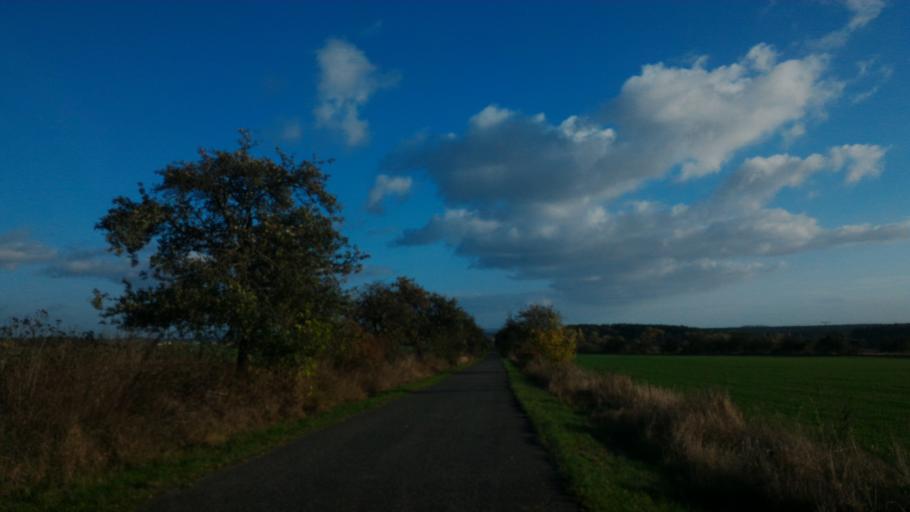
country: CZ
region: Central Bohemia
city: Bela pod Bezdezem
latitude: 50.5283
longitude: 14.7320
